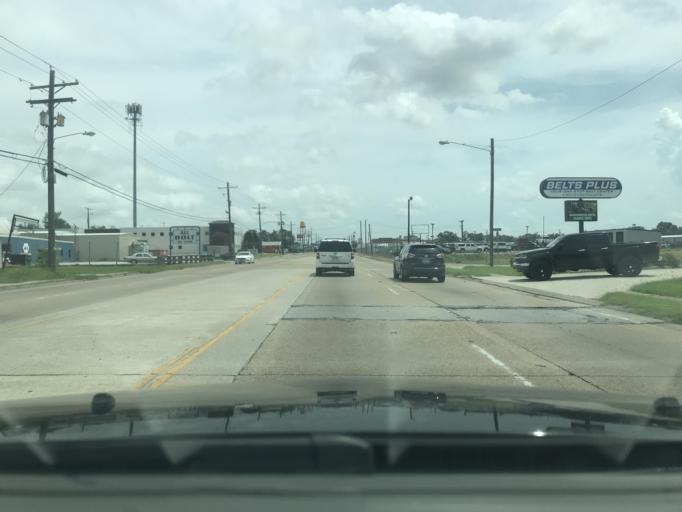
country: US
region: Louisiana
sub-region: Calcasieu Parish
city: Lake Charles
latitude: 30.2308
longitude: -93.1802
